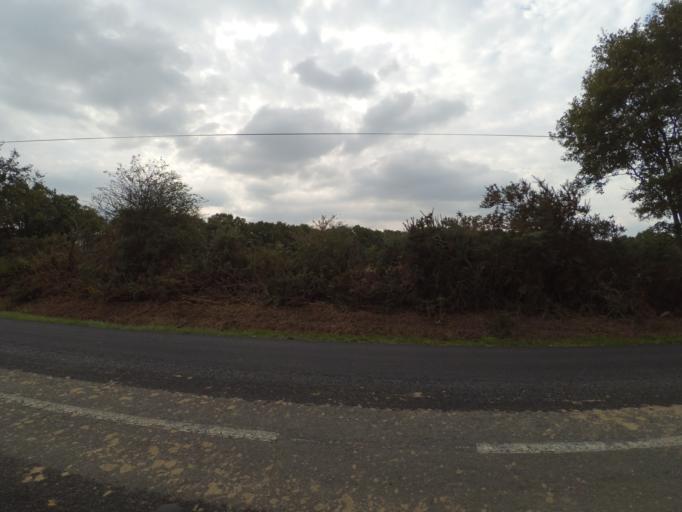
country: FR
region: Pays de la Loire
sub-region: Departement de la Vendee
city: Saint-Hilaire-de-Loulay
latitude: 46.9890
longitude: -1.3621
